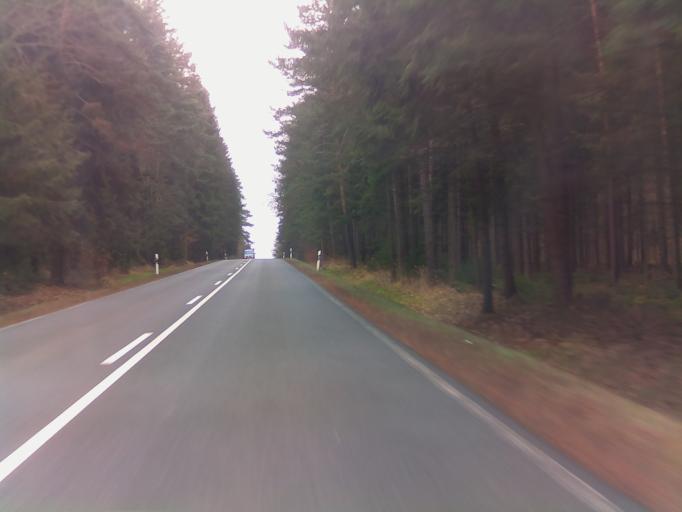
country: DE
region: Saxony
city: Pausa
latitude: 50.6151
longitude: 11.9970
